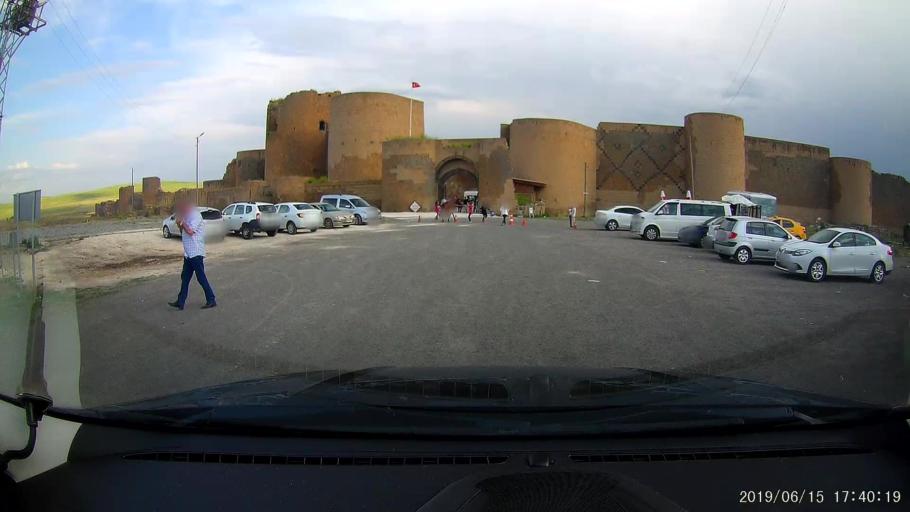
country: TR
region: Kars
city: Basgedikler
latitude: 40.5127
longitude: 43.5723
